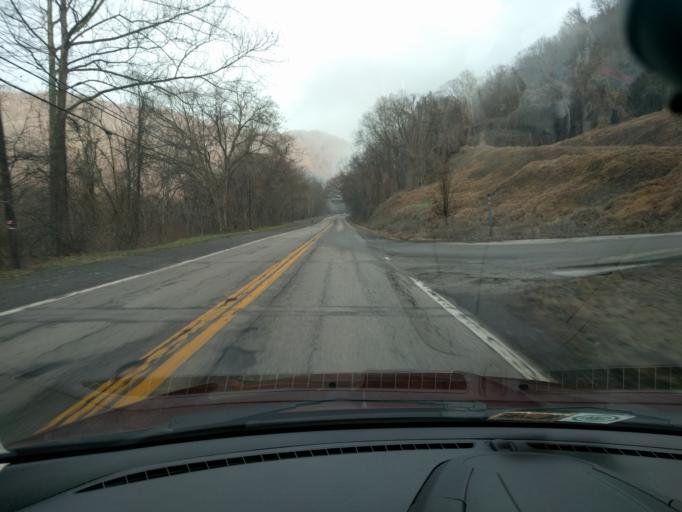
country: US
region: West Virginia
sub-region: Kanawha County
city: Montgomery
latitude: 38.1582
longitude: -81.2956
